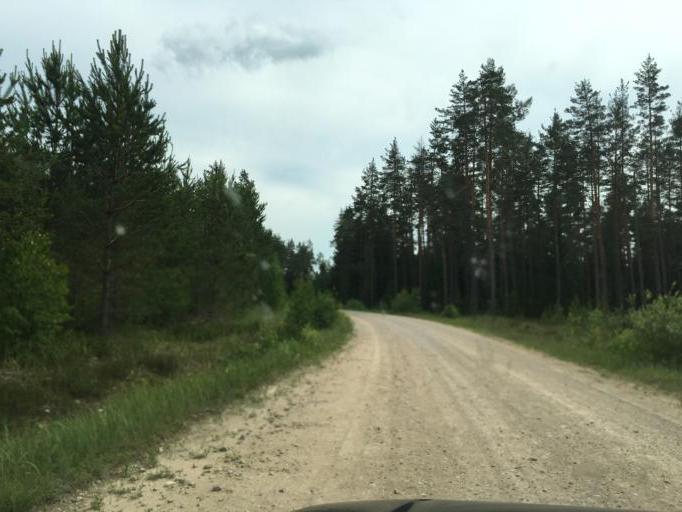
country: LV
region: Rugaju
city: Rugaji
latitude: 56.7695
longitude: 27.1050
